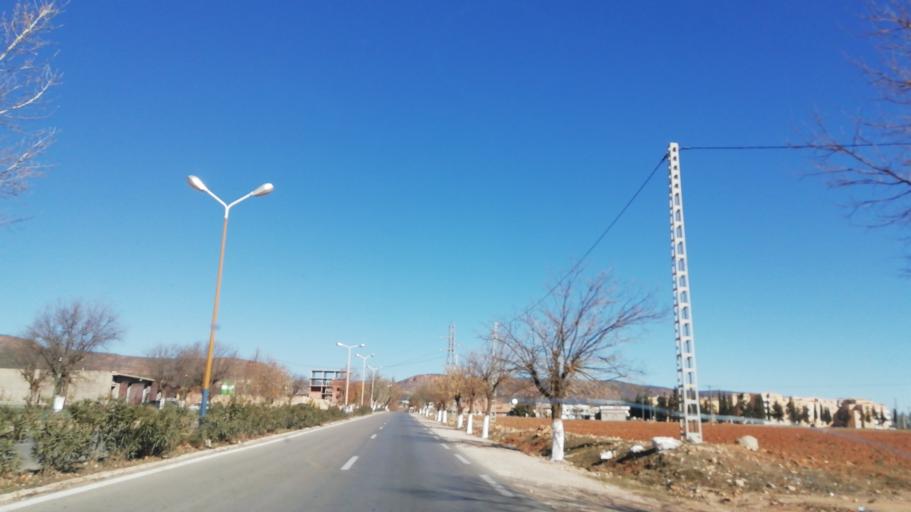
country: DZ
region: Tlemcen
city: Sebdou
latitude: 34.6603
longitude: -1.3233
